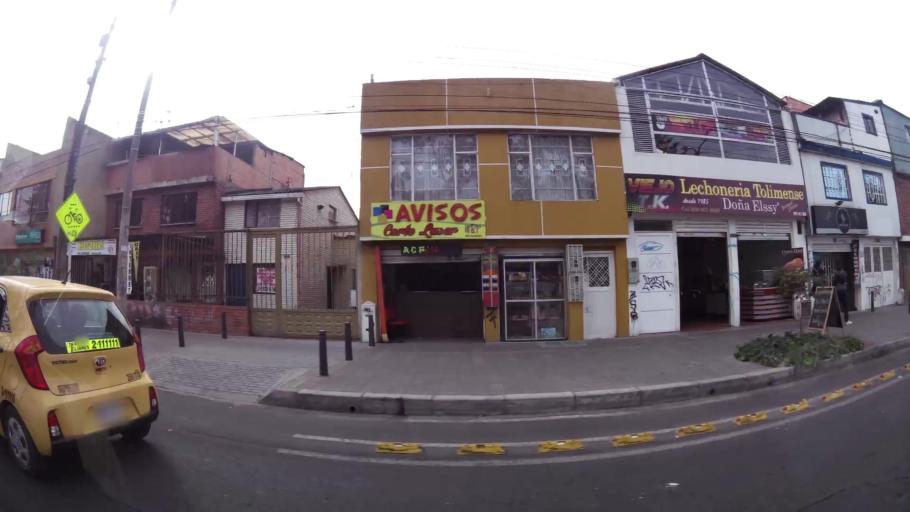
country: CO
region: Bogota D.C.
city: Bogota
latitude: 4.6279
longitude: -74.1499
